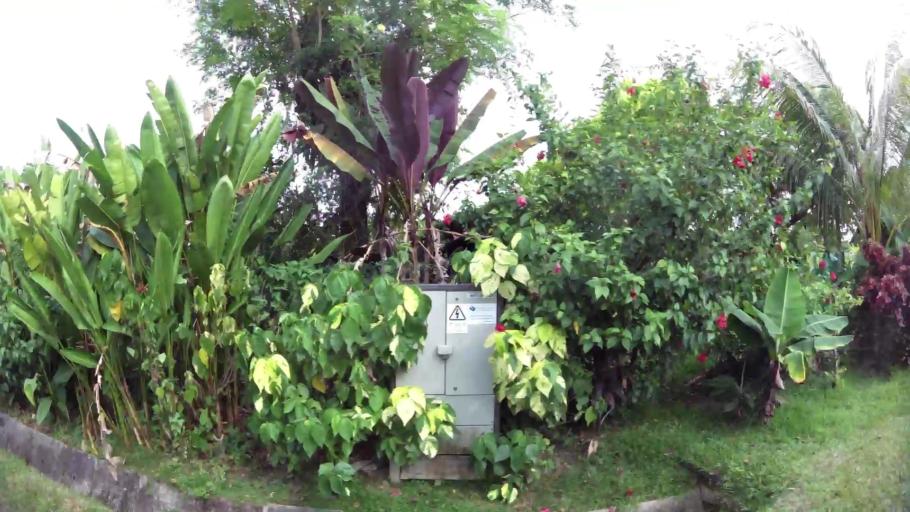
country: MY
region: Johor
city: Johor Bahru
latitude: 1.4190
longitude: 103.7162
